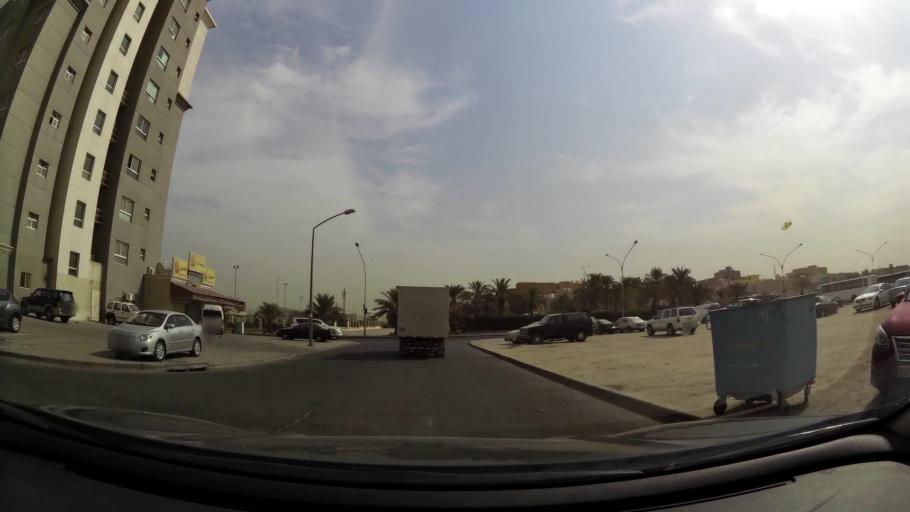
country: KW
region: Al Farwaniyah
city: Janub as Surrah
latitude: 29.2808
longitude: 47.9767
